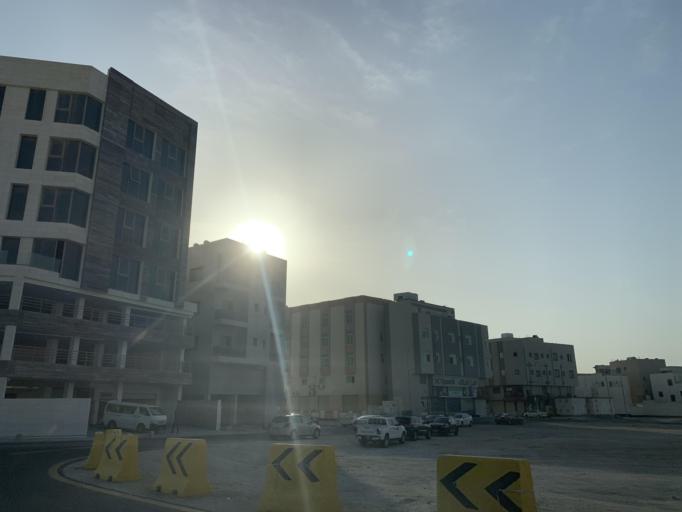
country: BH
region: Muharraq
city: Al Muharraq
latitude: 26.2812
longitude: 50.5972
